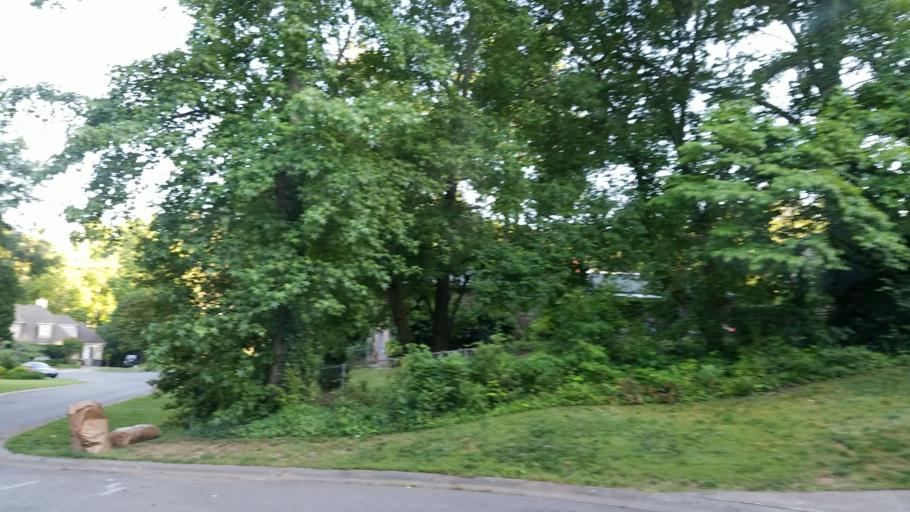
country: US
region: Georgia
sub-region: Cobb County
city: Vinings
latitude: 33.8742
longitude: -84.4833
